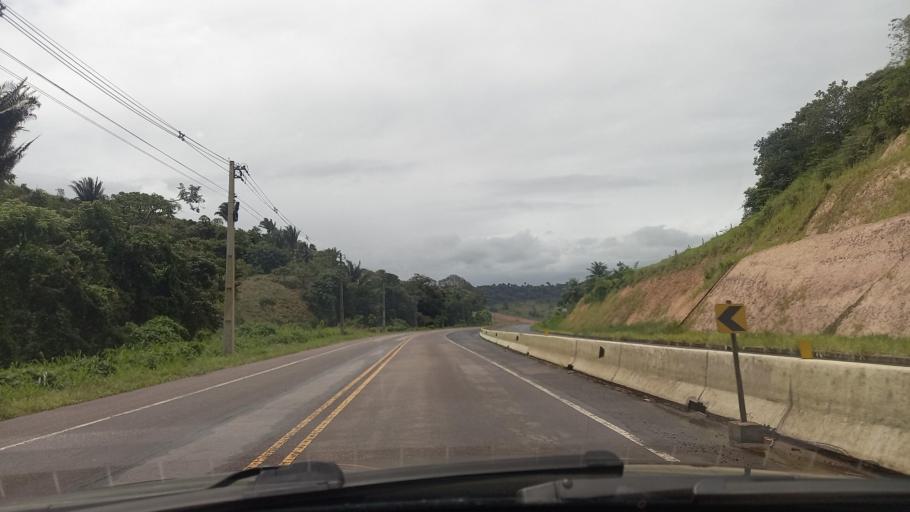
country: BR
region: Alagoas
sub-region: Campo Alegre
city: Campo Alegre
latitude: -9.8214
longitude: -36.2240
